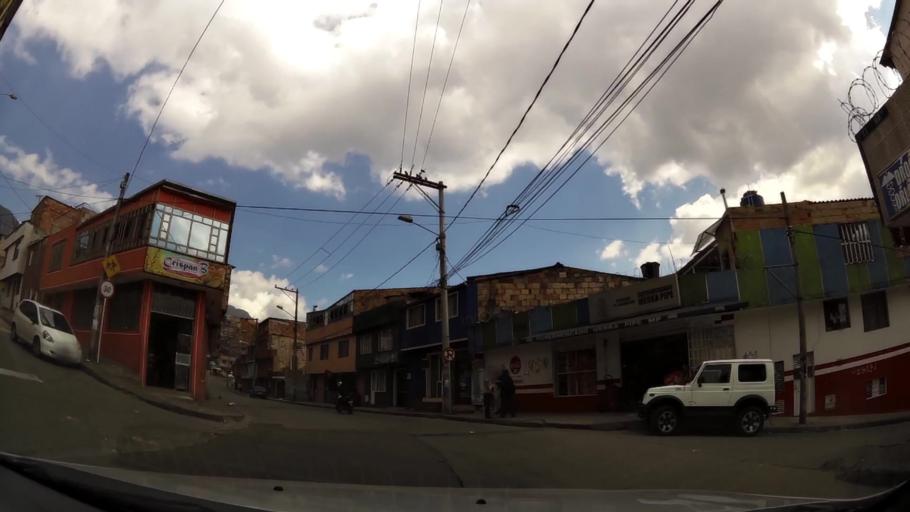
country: CO
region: Bogota D.C.
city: Bogota
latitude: 4.5575
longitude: -74.0911
